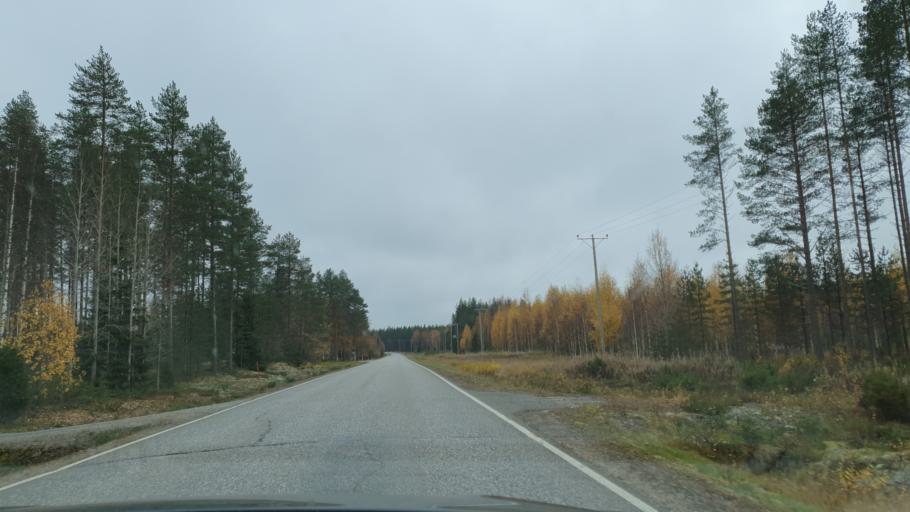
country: FI
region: Kainuu
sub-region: Kajaani
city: Sotkamo
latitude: 64.2573
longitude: 28.4986
